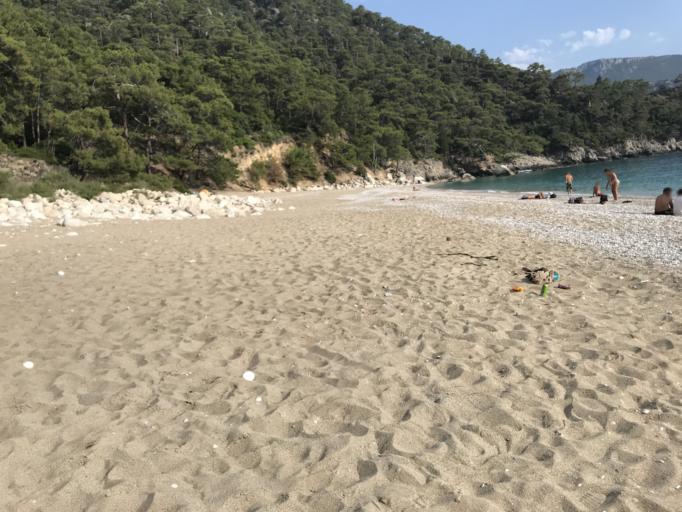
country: TR
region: Mugla
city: OEluedeniz
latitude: 36.4416
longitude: 29.1310
